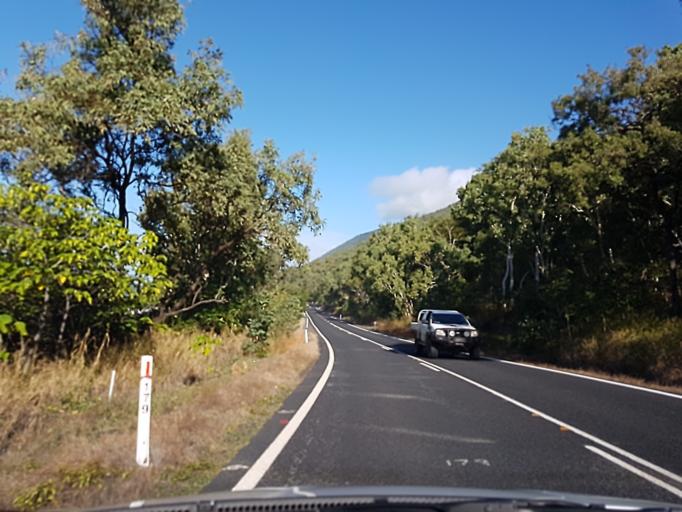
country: AU
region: Queensland
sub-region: Cairns
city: Palm Cove
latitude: -16.7088
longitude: 145.6308
